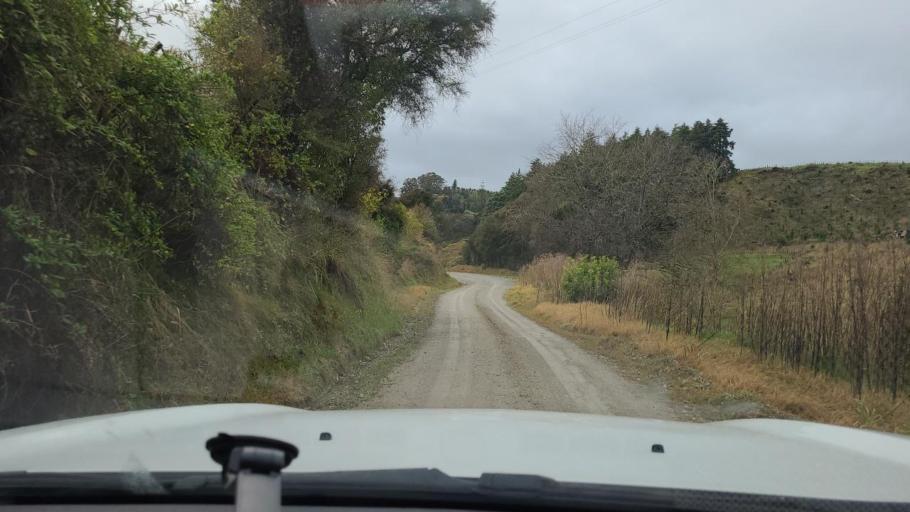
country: NZ
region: Gisborne
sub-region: Gisborne District
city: Gisborne
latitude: -38.5670
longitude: 177.7868
